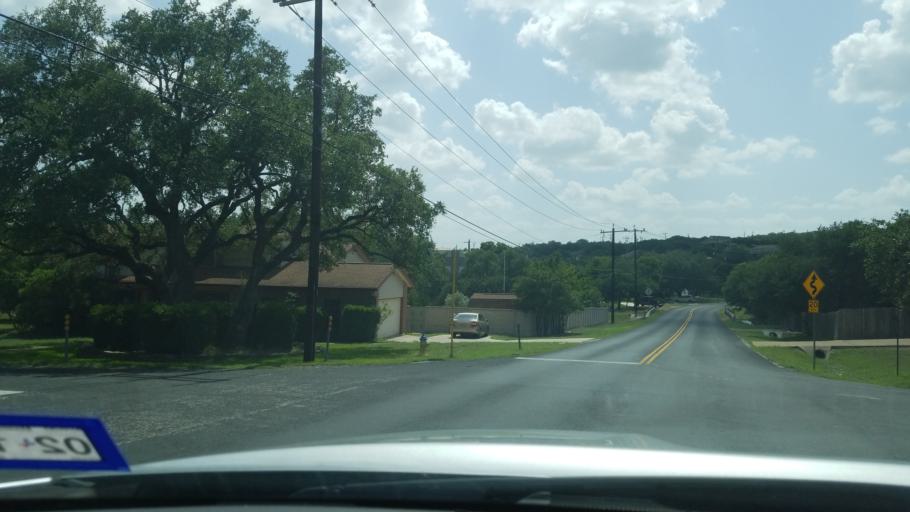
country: US
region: Texas
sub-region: Bexar County
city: Timberwood Park
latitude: 29.6850
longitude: -98.4854
